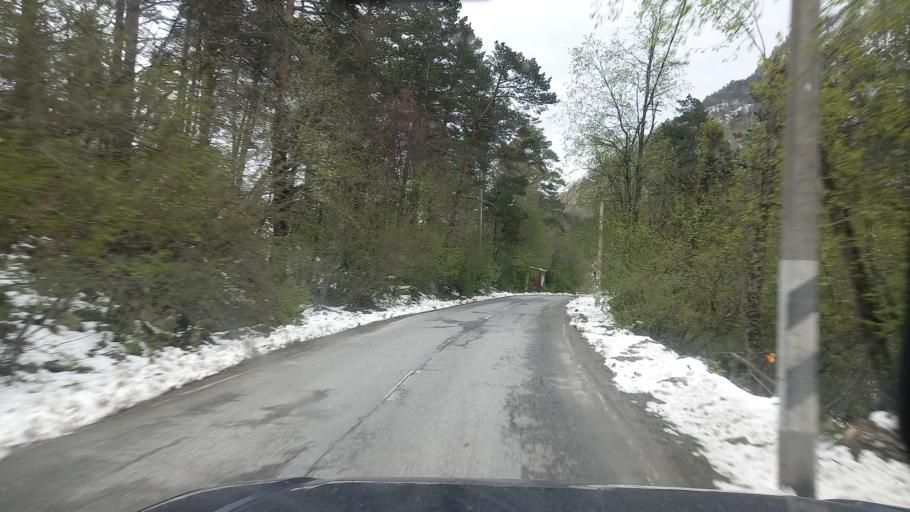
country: RU
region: North Ossetia
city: Mizur
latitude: 42.7930
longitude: 43.9204
